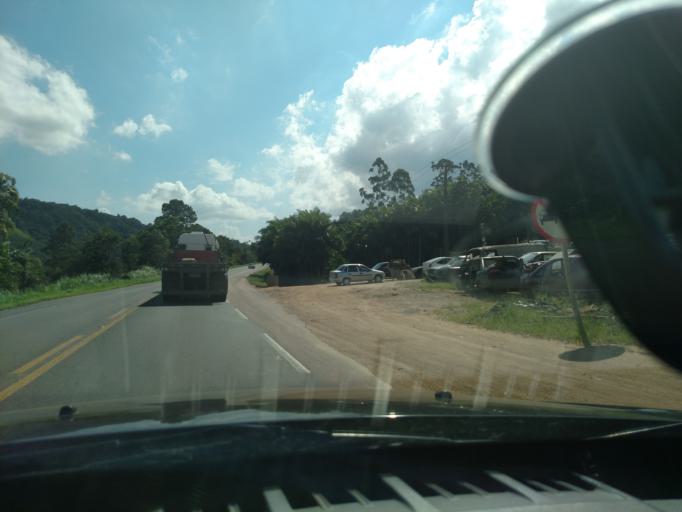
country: BR
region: Santa Catarina
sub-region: Rodeio
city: Gavea
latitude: -26.9511
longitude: -49.3026
